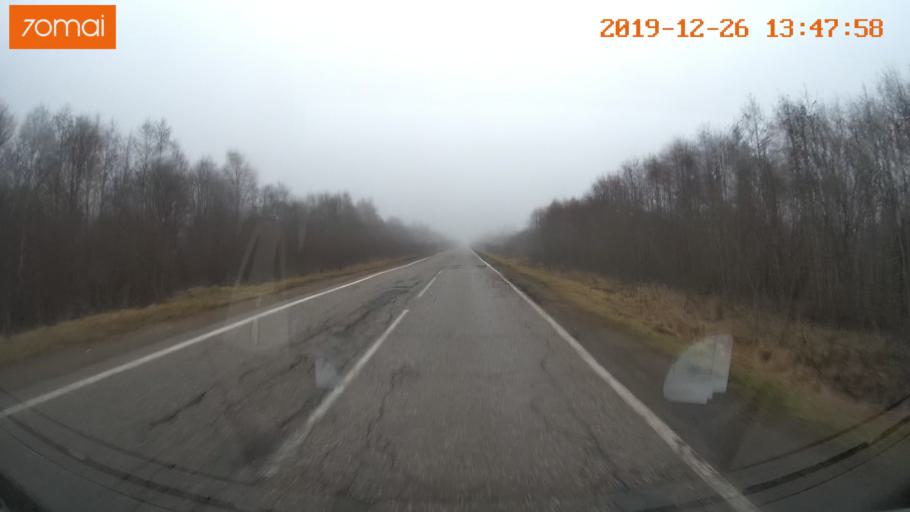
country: RU
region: Vologda
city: Sheksna
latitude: 58.6804
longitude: 38.5410
